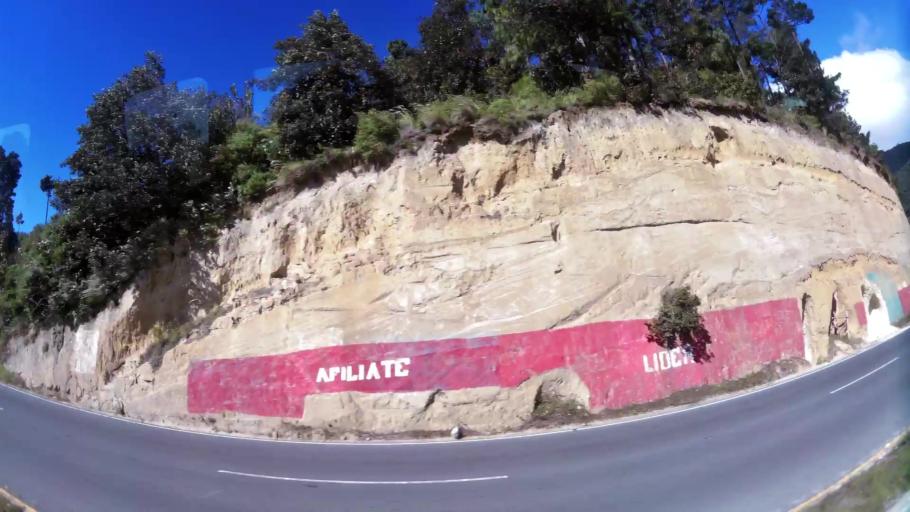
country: GT
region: Solola
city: Concepcion
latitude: 14.8289
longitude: -91.1835
